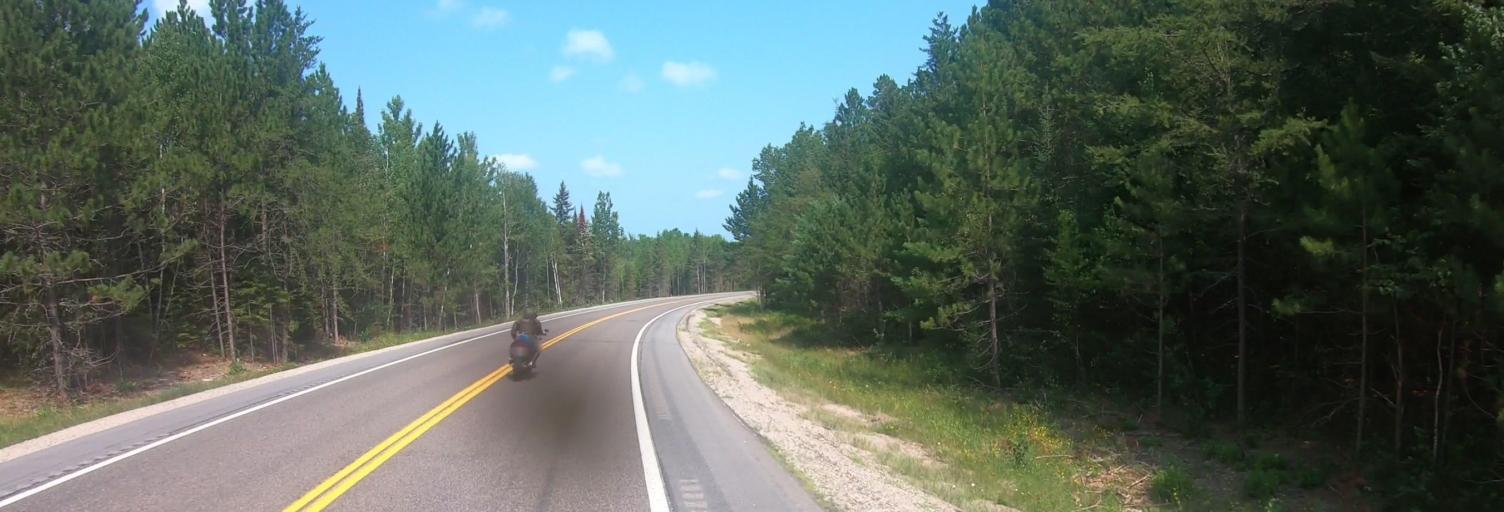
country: US
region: Minnesota
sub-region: Saint Louis County
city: Parkville
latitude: 48.1662
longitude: -92.5277
